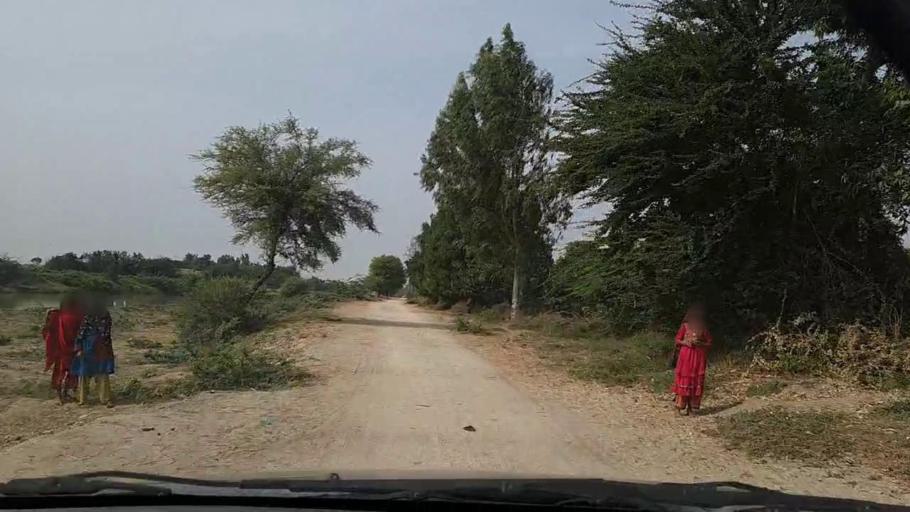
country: PK
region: Sindh
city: Thatta
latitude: 24.5692
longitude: 67.8600
